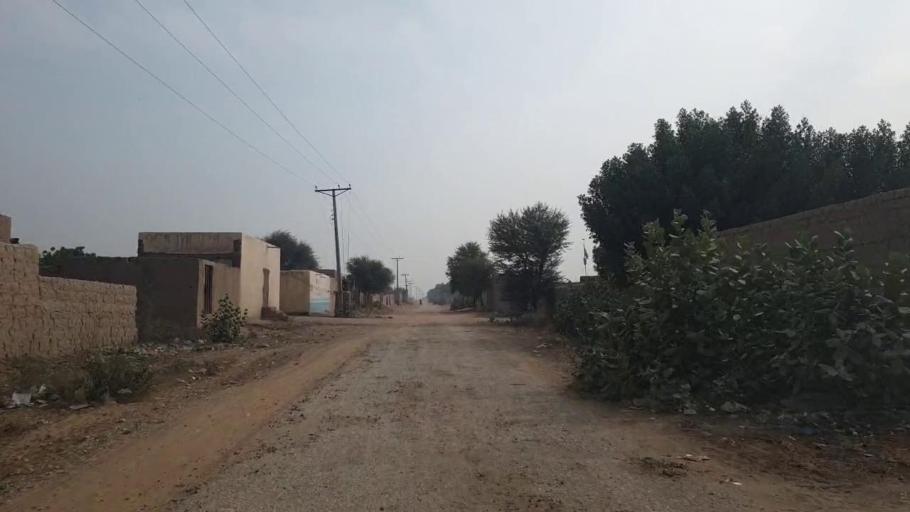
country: PK
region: Sindh
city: Sann
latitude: 26.0345
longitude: 68.1335
